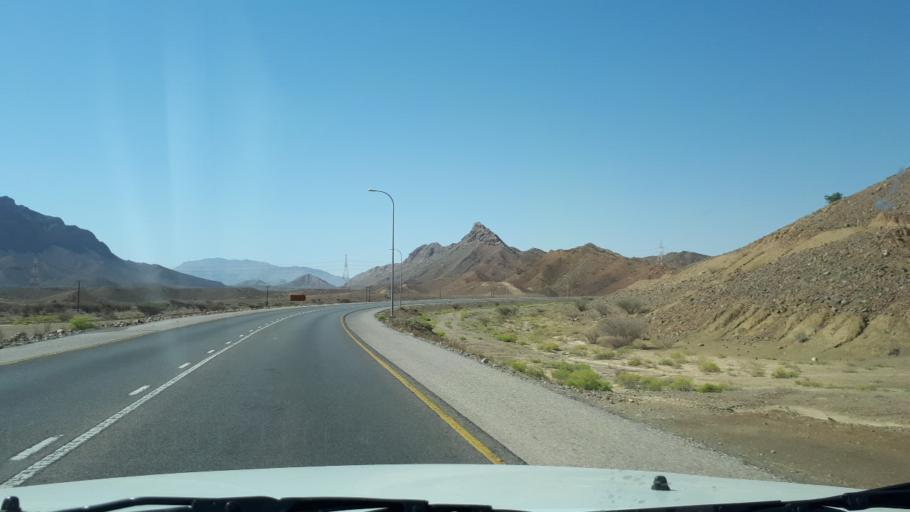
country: OM
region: Ash Sharqiyah
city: Sur
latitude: 22.3431
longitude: 59.3145
